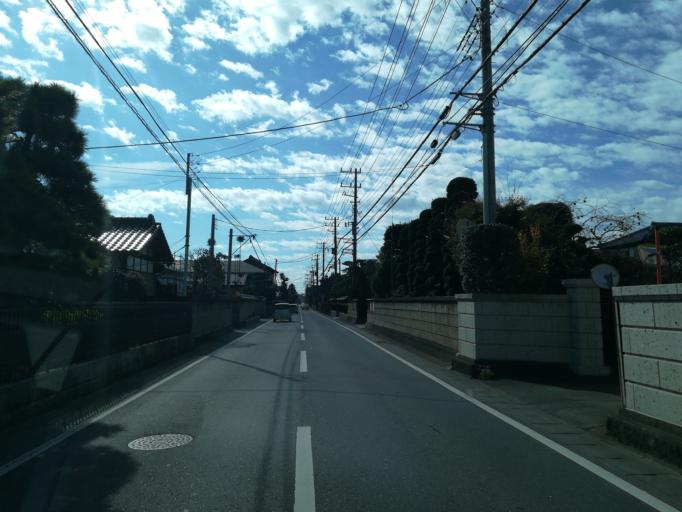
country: JP
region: Ibaraki
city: Naka
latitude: 36.0806
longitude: 140.1008
